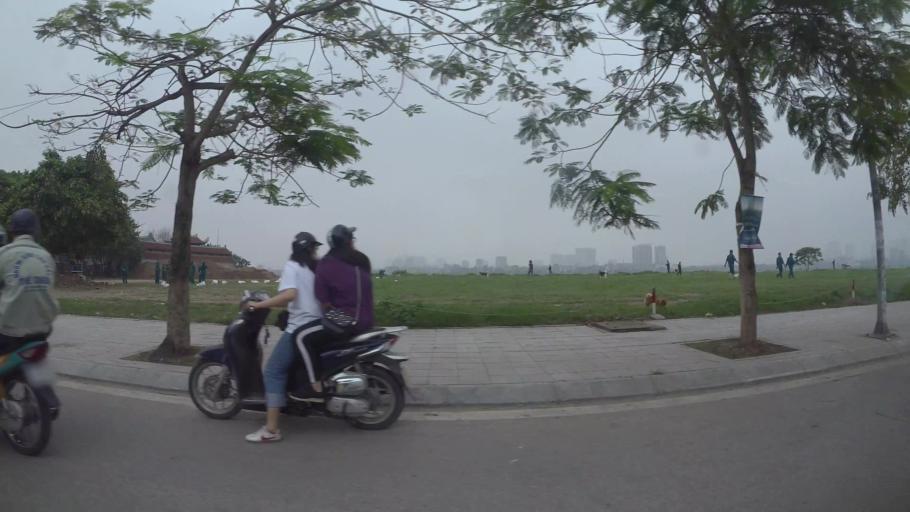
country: VN
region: Ha Noi
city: Tay Ho
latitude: 21.0577
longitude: 105.8197
